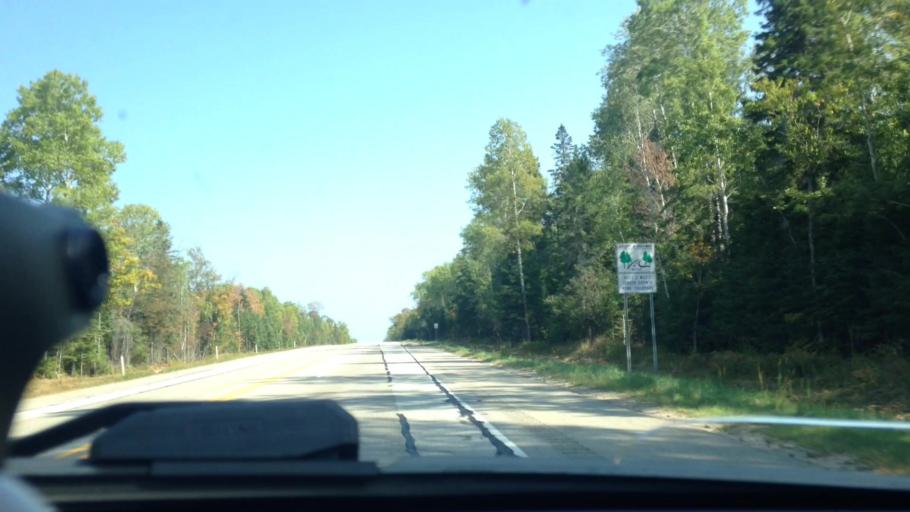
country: US
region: Michigan
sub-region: Luce County
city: Newberry
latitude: 46.3036
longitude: -85.2954
